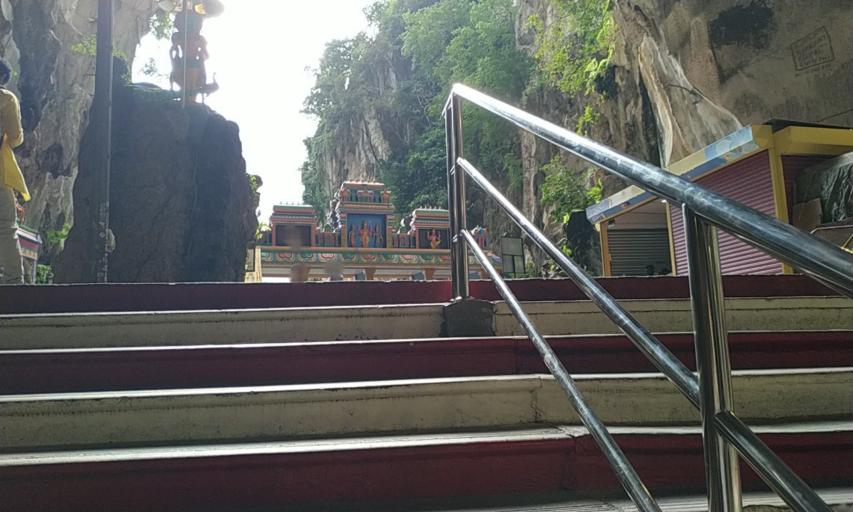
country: MY
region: Kuala Lumpur
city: Kuala Lumpur
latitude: 3.2382
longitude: 101.6847
